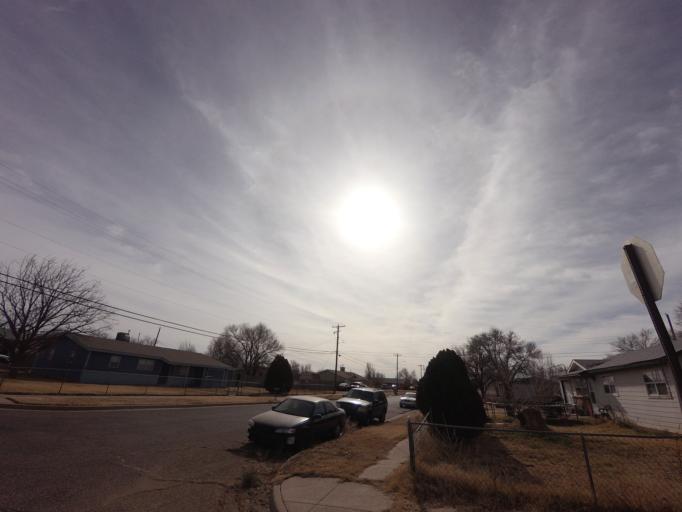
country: US
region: New Mexico
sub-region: Curry County
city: Clovis
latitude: 34.4098
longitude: -103.2449
